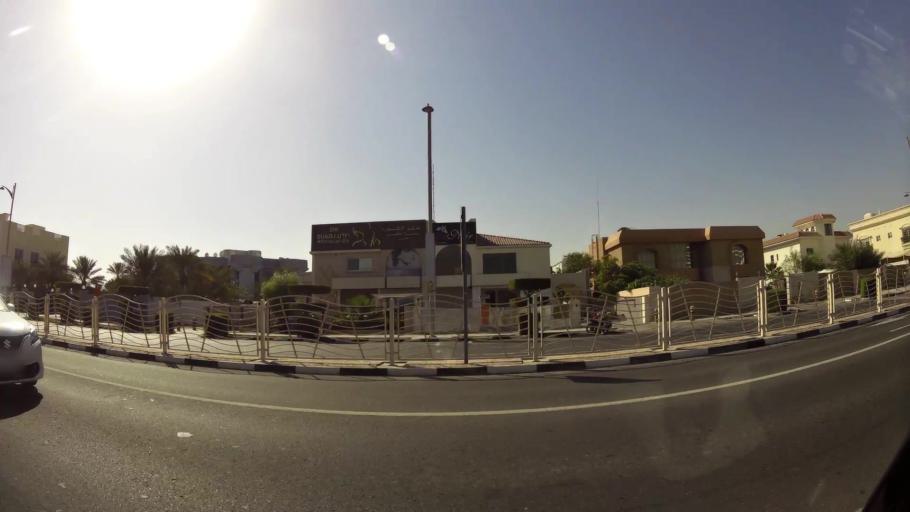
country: AE
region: Dubai
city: Dubai
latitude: 25.1429
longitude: 55.1931
